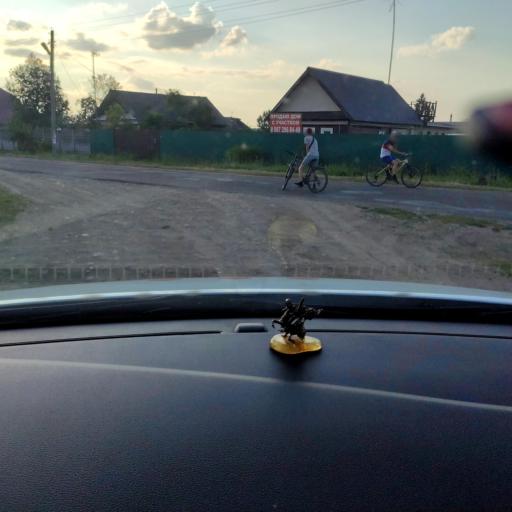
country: RU
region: Tatarstan
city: Pestretsy
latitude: 55.6156
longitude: 49.4958
